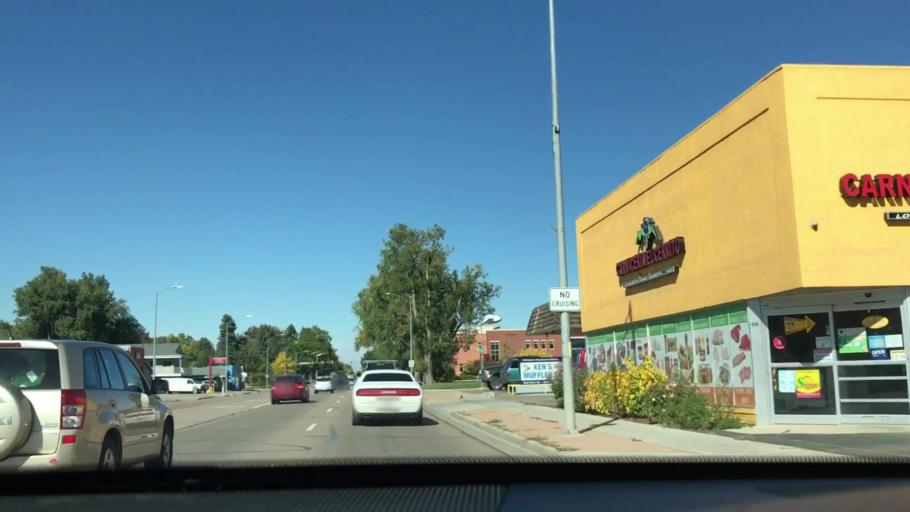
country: US
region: Colorado
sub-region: Boulder County
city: Longmont
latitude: 40.1752
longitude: -105.1024
